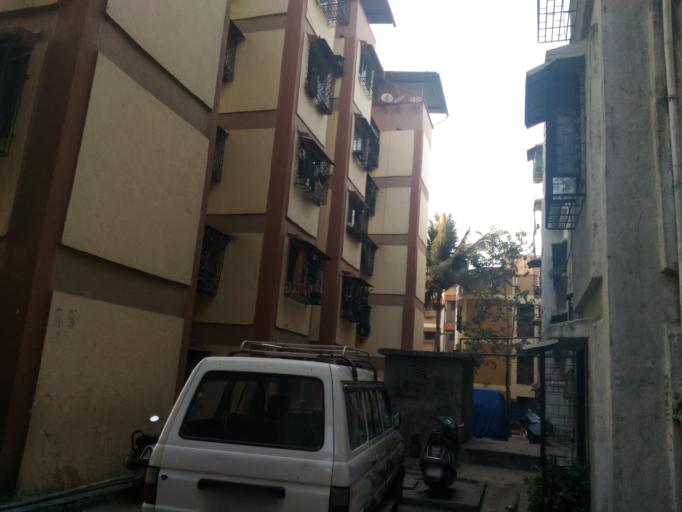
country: IN
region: Maharashtra
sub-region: Thane
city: Bhayandar
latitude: 19.3128
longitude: 72.8561
